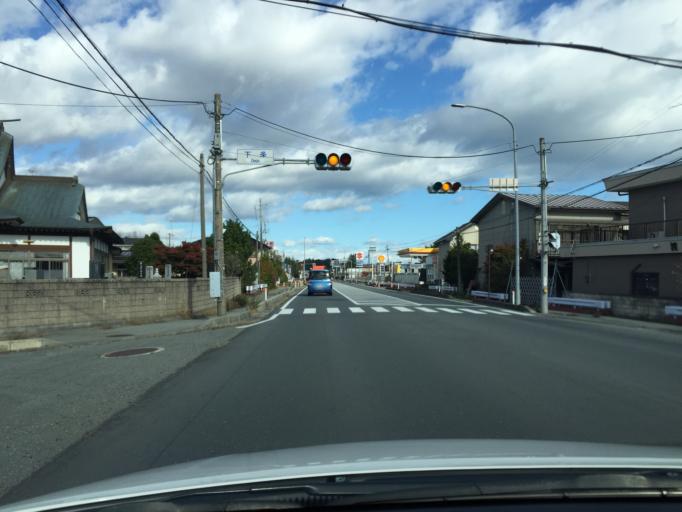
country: JP
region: Fukushima
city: Namie
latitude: 37.4482
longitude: 141.0087
